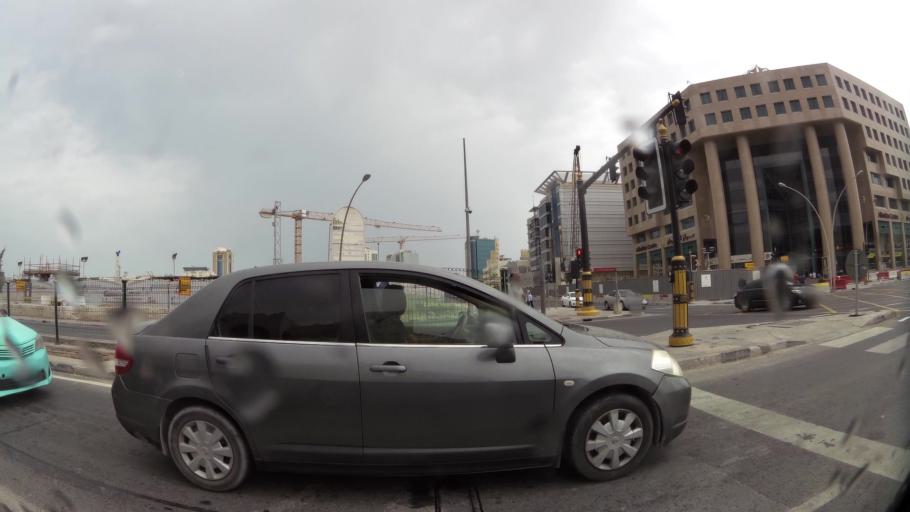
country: QA
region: Baladiyat ad Dawhah
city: Doha
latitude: 25.2864
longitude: 51.5347
